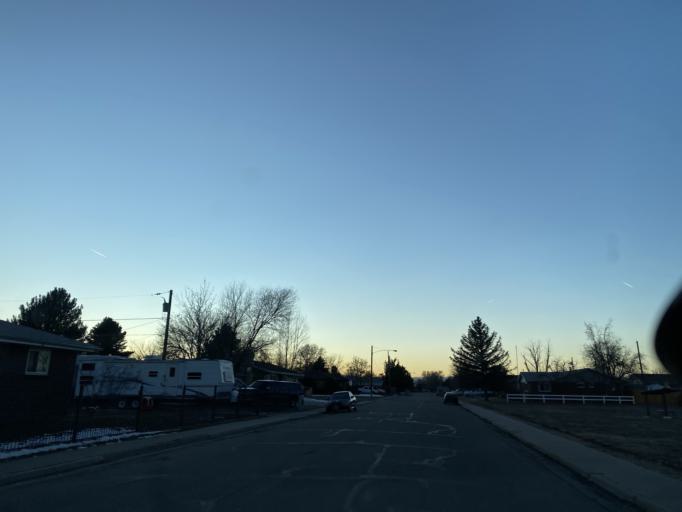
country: US
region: Colorado
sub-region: Adams County
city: Brighton
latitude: 39.9760
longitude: -104.8127
